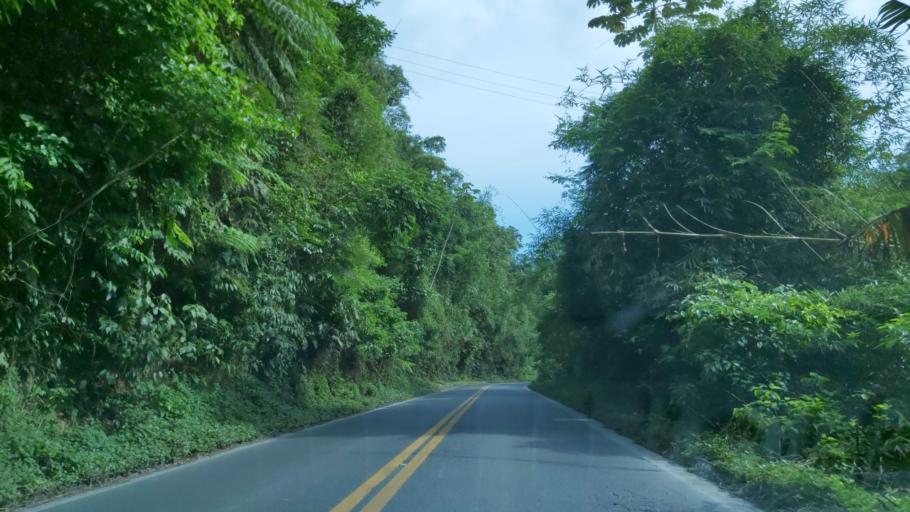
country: BR
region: Sao Paulo
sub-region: Juquia
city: Juquia
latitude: -24.0828
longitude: -47.6078
